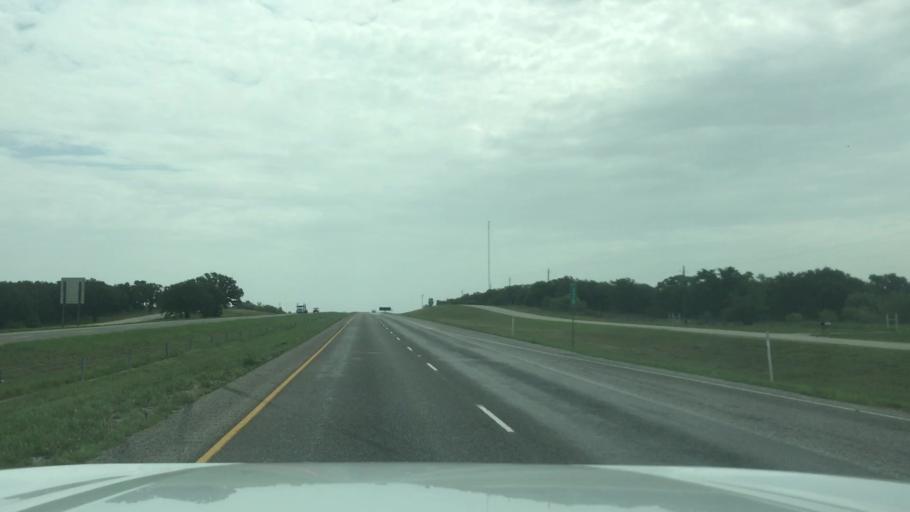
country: US
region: Texas
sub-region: Eastland County
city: Eastland
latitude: 32.3755
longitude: -98.8775
